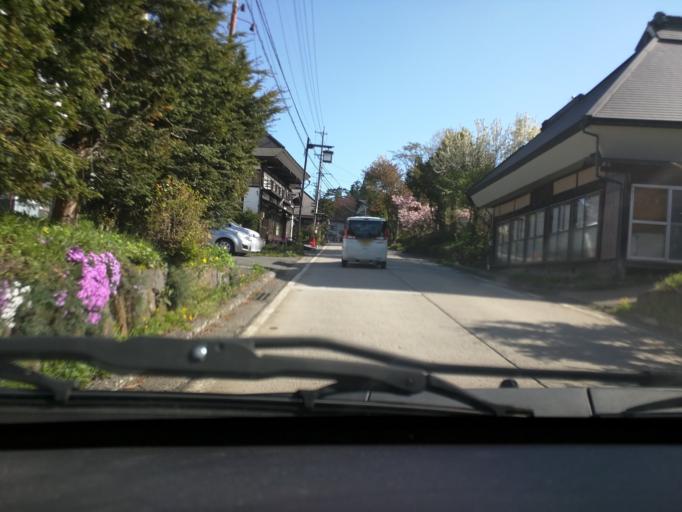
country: JP
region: Nagano
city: Nagano-shi
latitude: 36.7373
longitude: 138.0852
